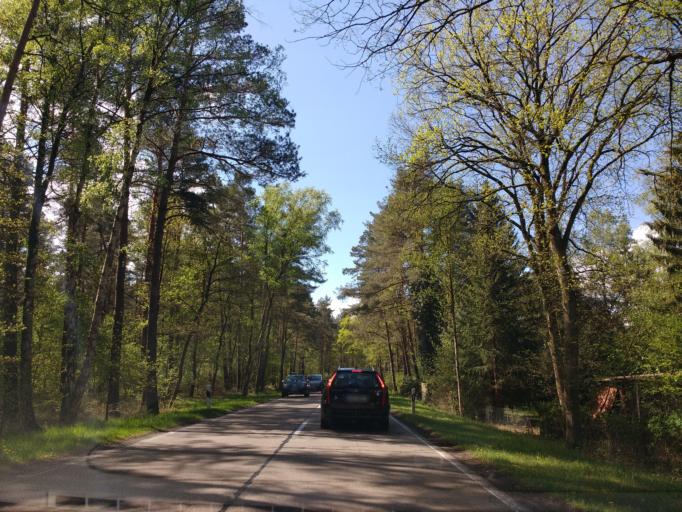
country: DE
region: Lower Saxony
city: Essel
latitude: 52.7079
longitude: 9.6772
